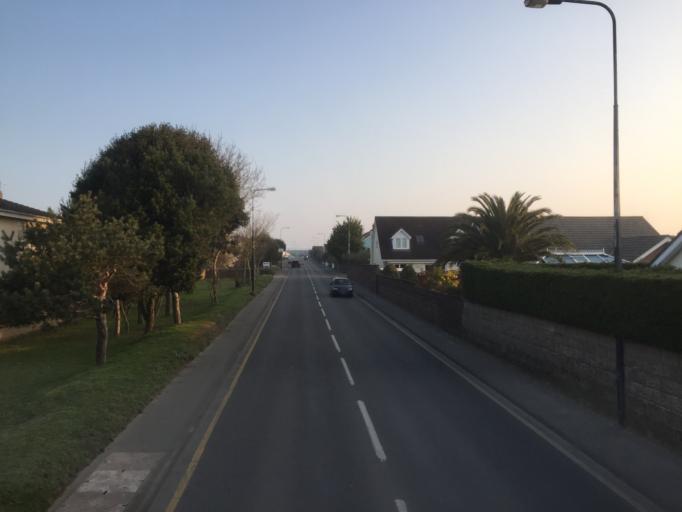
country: JE
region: St Helier
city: Saint Helier
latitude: 49.1956
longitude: -2.1985
